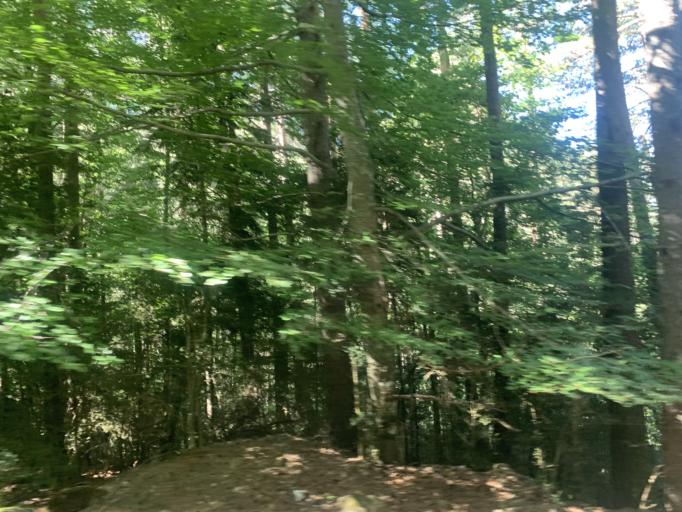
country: ES
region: Aragon
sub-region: Provincia de Huesca
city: Broto
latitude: 42.6544
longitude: -0.0791
